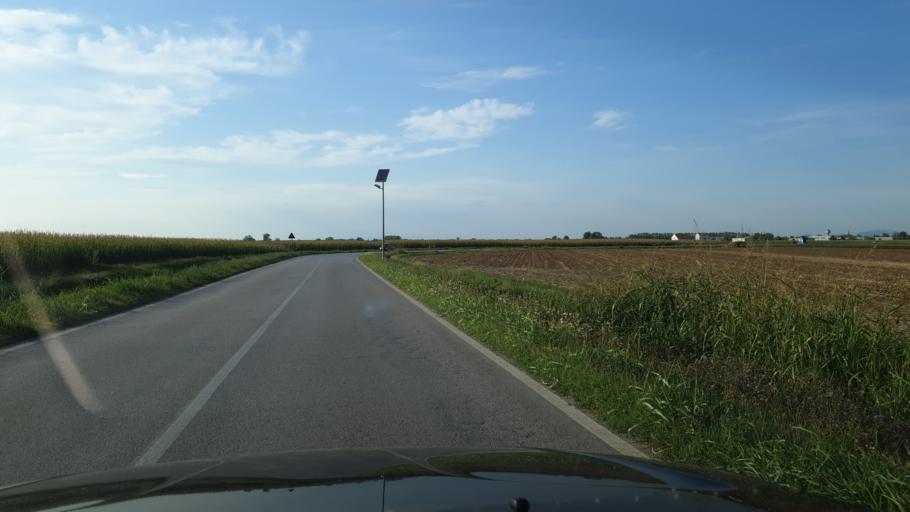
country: IT
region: Veneto
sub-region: Provincia di Rovigo
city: Fiesso Umbertiano
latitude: 44.9741
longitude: 11.6085
